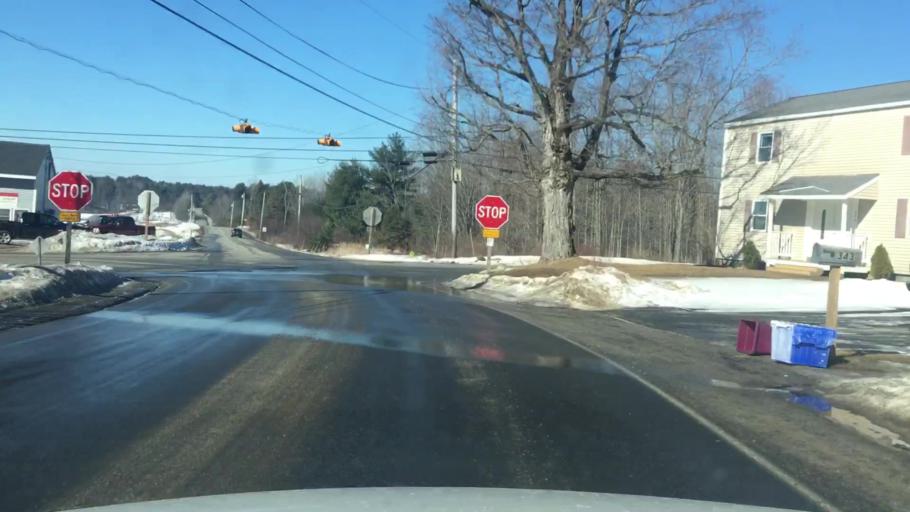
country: US
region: Maine
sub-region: Cumberland County
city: North Windham
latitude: 43.8246
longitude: -70.3883
